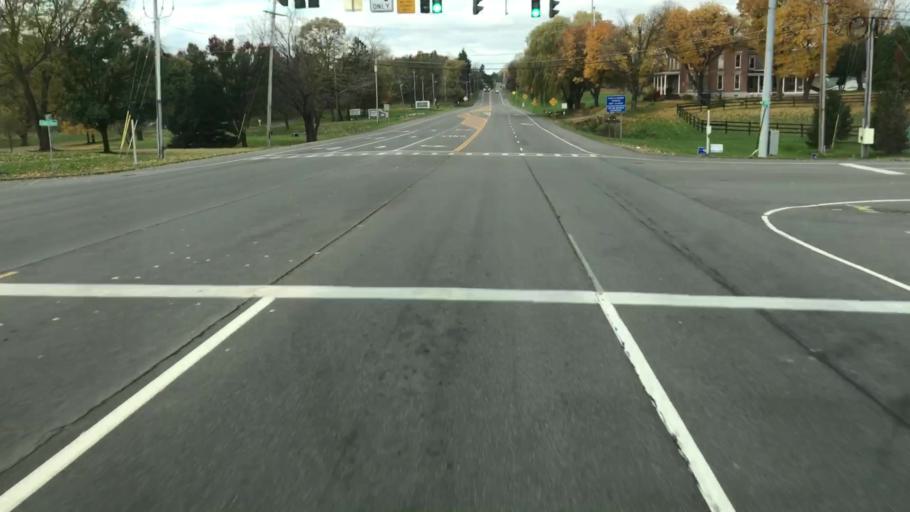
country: US
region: New York
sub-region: Onondaga County
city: Camillus
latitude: 43.0364
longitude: -76.3344
